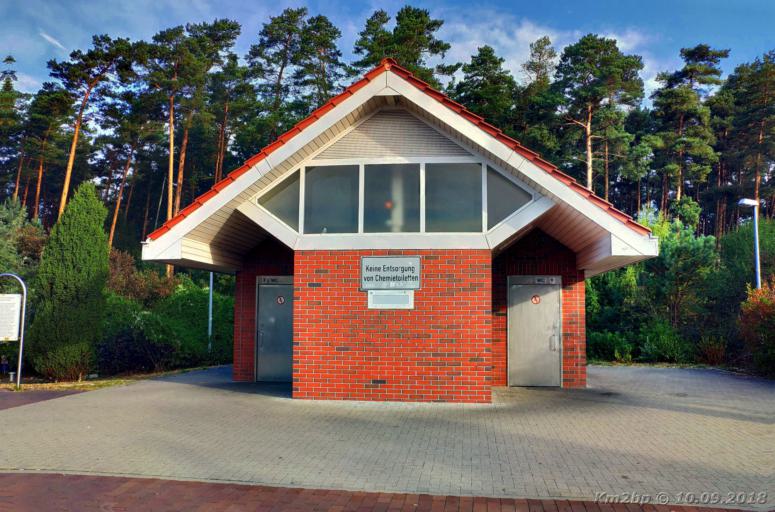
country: DE
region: Brandenburg
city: Wildau
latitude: 52.3235
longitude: 13.7056
